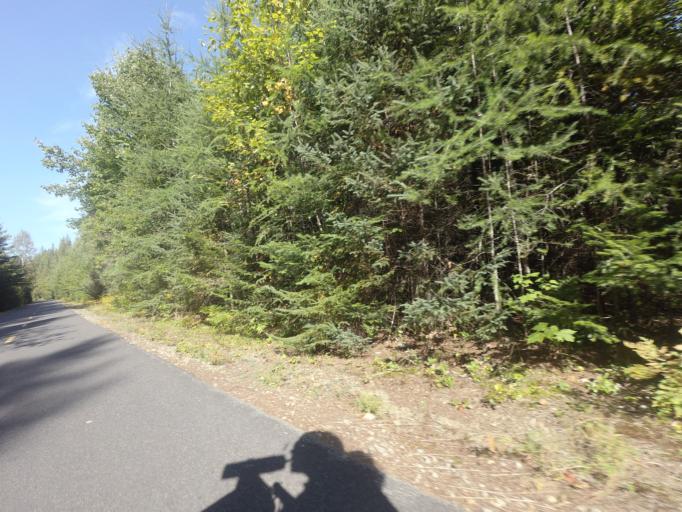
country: CA
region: Quebec
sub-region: Laurentides
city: Mont-Tremblant
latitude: 46.1199
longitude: -74.5190
